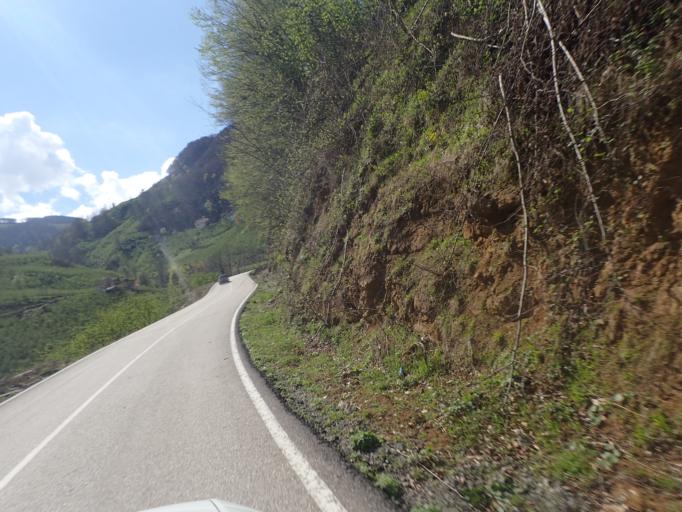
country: TR
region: Ordu
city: Korgan
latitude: 40.7685
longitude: 37.3256
